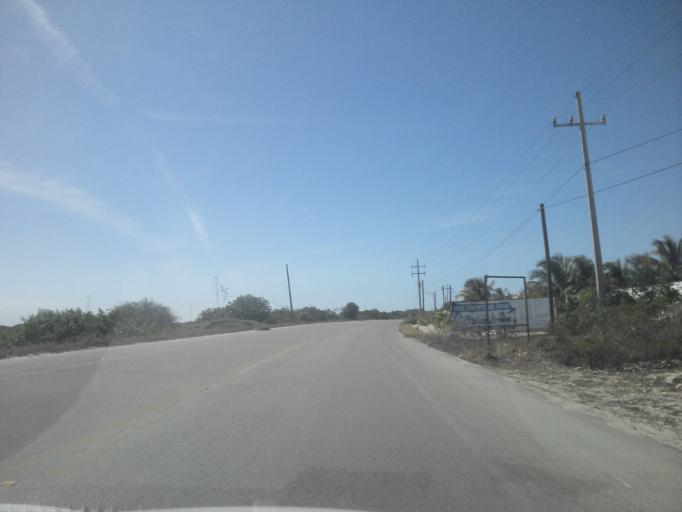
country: MX
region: Yucatan
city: Telchac Puerto
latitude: 21.3315
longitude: -89.3612
